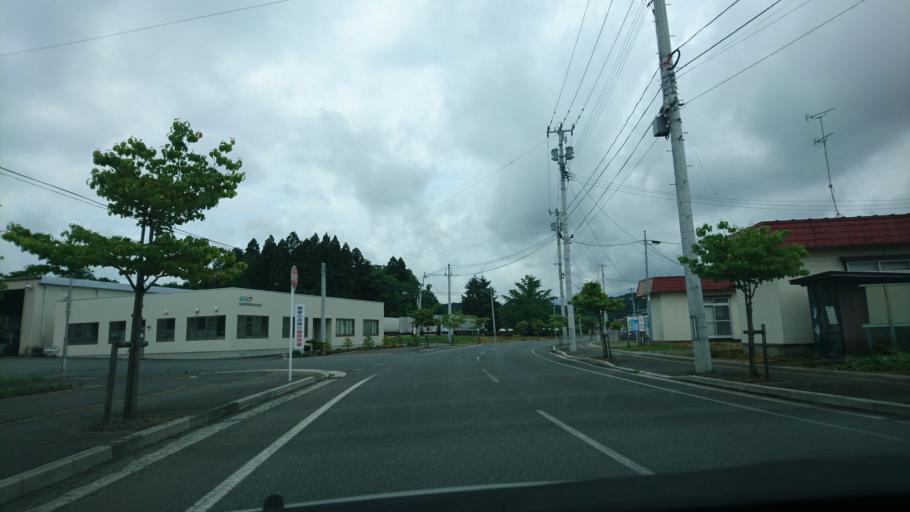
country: JP
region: Iwate
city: Ichinoseki
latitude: 38.9342
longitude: 141.0872
